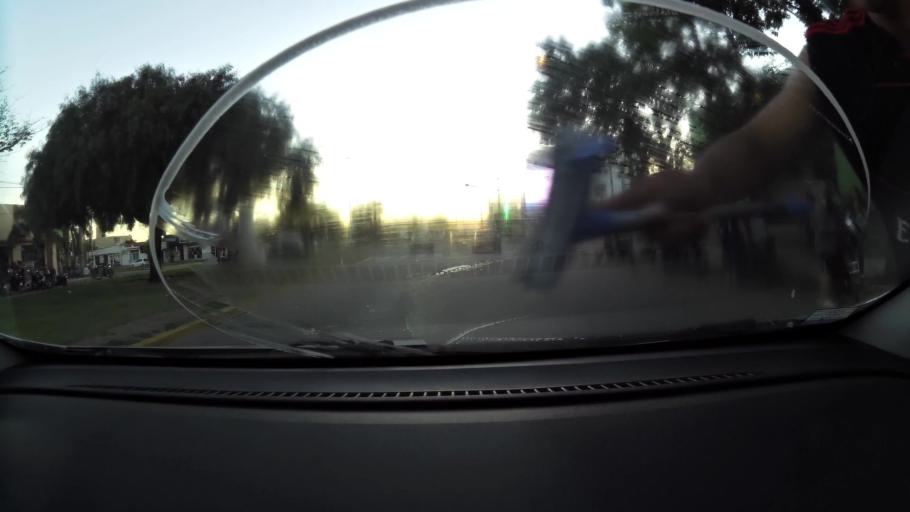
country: AR
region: Cordoba
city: Villa Maria
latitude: -32.4088
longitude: -63.2564
